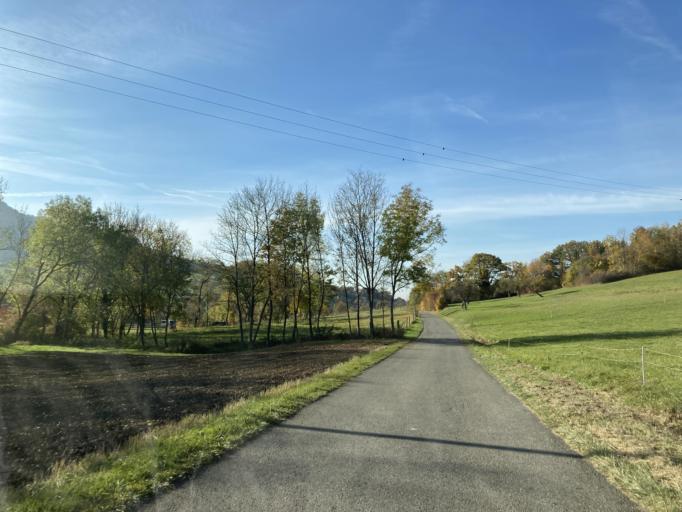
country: DE
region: Baden-Wuerttemberg
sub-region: Tuebingen Region
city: Nehren
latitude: 48.3927
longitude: 9.1049
